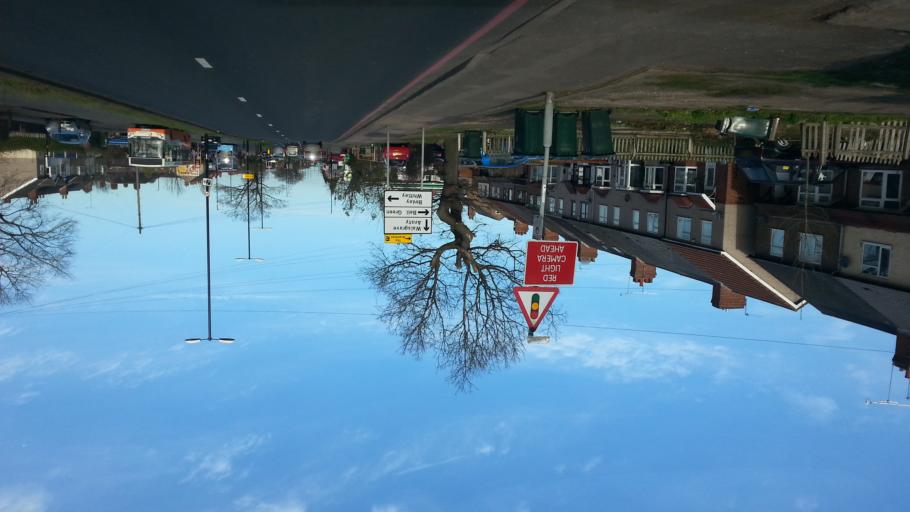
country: GB
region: England
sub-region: Coventry
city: Coventry
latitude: 52.4162
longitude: -1.4626
